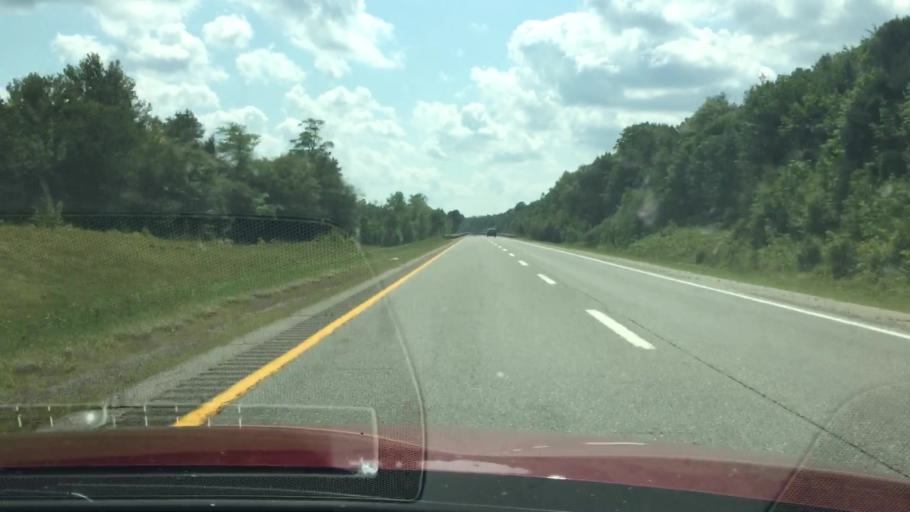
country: US
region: Maine
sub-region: Penobscot County
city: Medway
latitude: 45.5589
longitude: -68.5489
